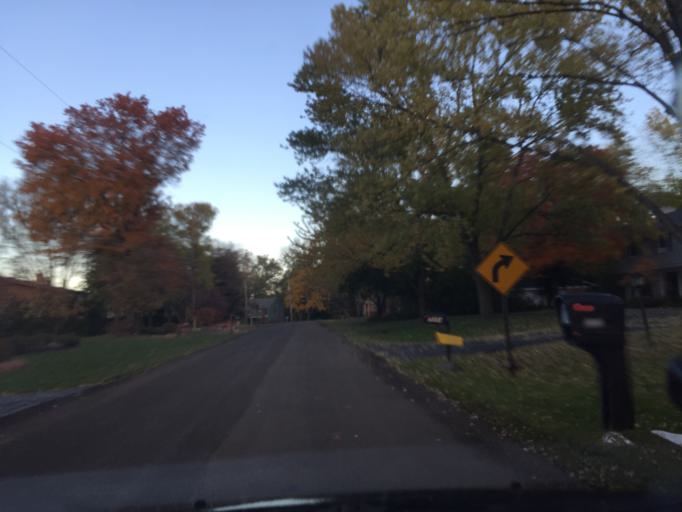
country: US
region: Michigan
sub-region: Oakland County
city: Franklin
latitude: 42.5612
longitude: -83.2886
